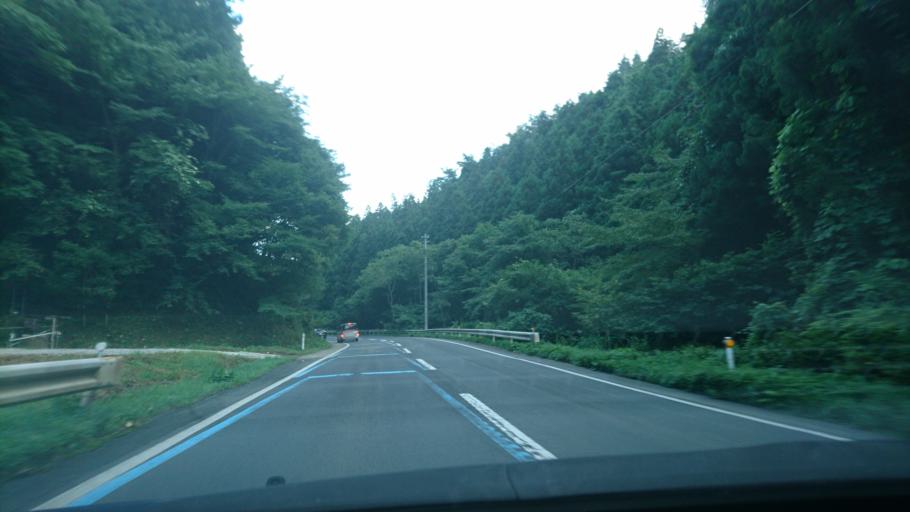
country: JP
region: Iwate
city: Mizusawa
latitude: 39.0418
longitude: 141.2433
